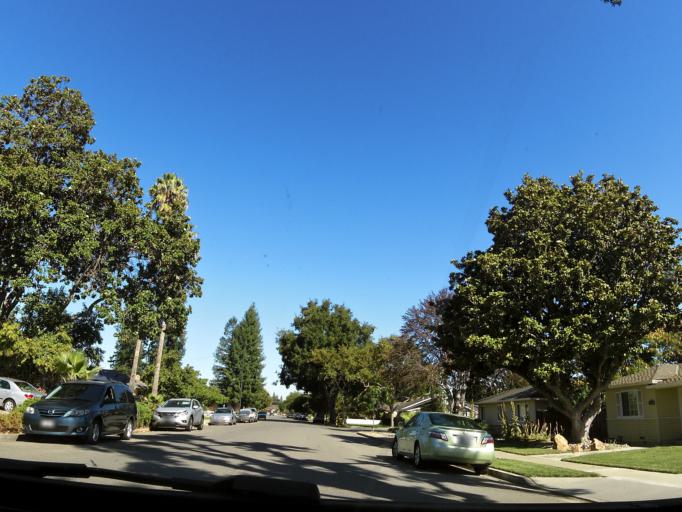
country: US
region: California
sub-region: Santa Clara County
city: Buena Vista
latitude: 37.2949
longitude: -121.9183
